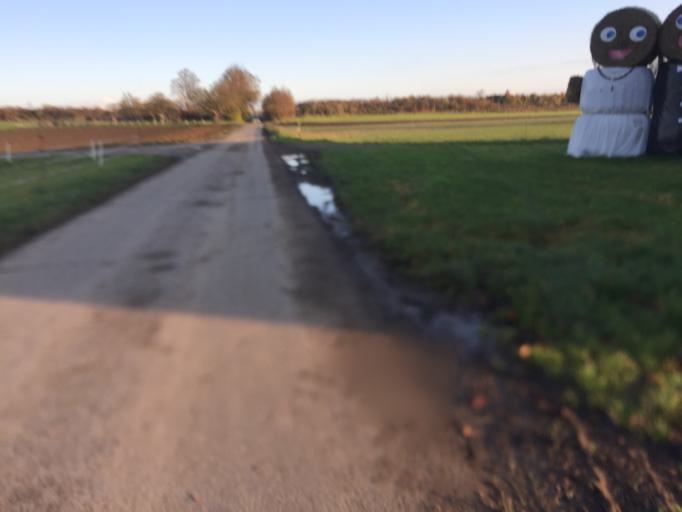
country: DE
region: Hesse
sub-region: Regierungsbezirk Darmstadt
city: Munzenberg
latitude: 50.4863
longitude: 8.7289
